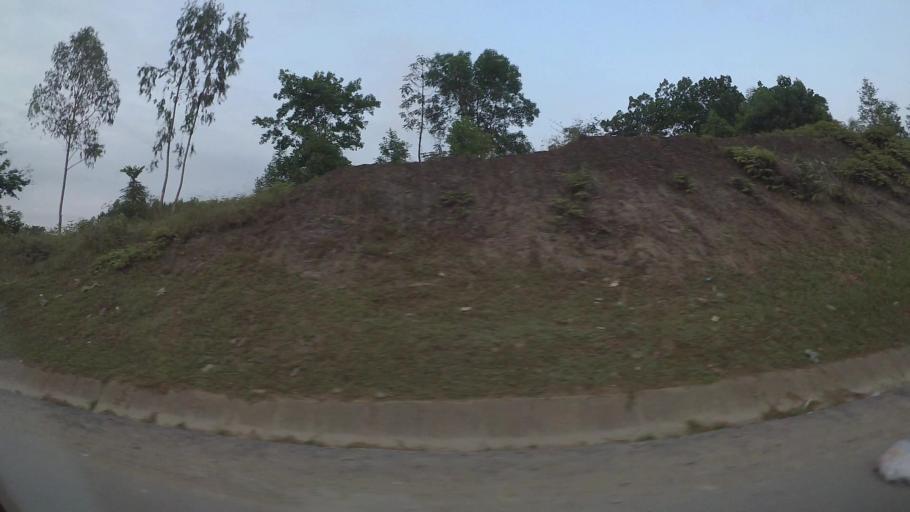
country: VN
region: Da Nang
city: Lien Chieu
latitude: 16.0527
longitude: 108.1039
